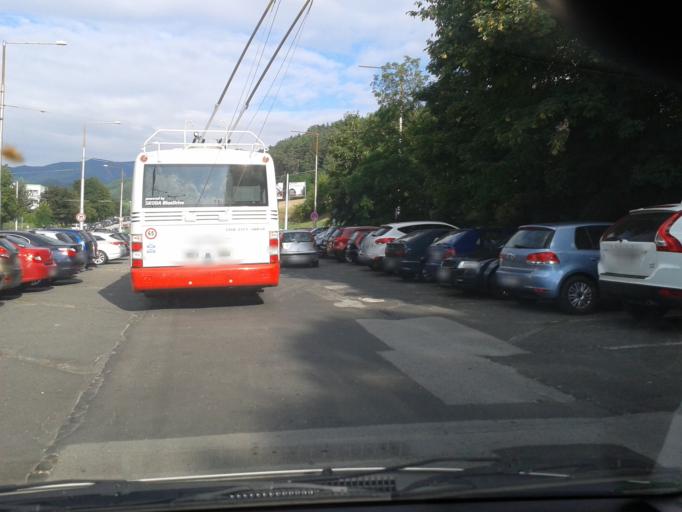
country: SK
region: Banskobystricky
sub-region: Okres Banska Bystrica
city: Banska Bystrica
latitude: 48.7448
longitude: 19.1178
